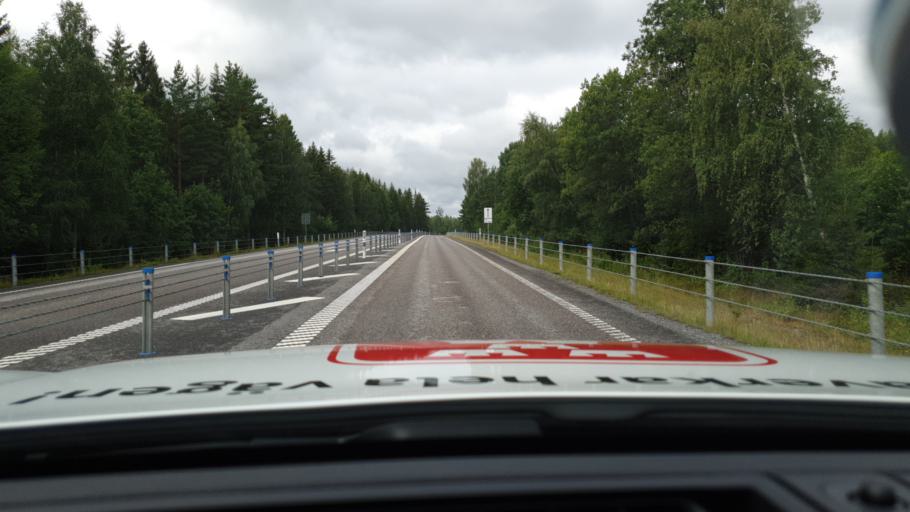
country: SE
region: Soedermanland
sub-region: Flens Kommun
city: Flen
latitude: 59.0381
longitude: 16.4746
